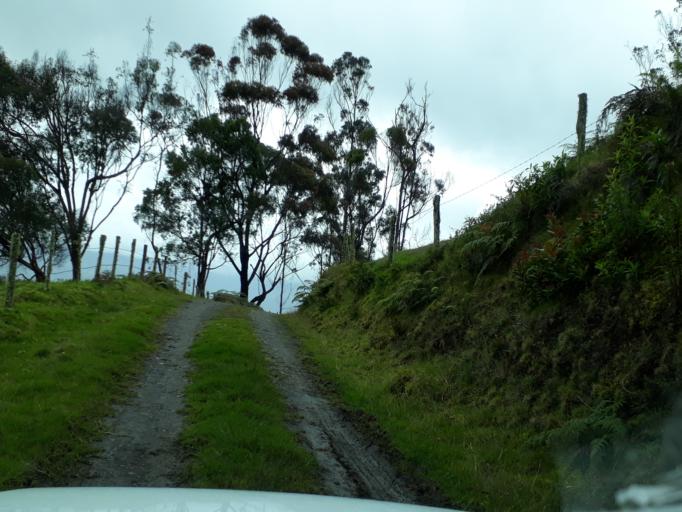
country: CO
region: Cundinamarca
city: Junin
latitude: 4.7363
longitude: -73.6257
